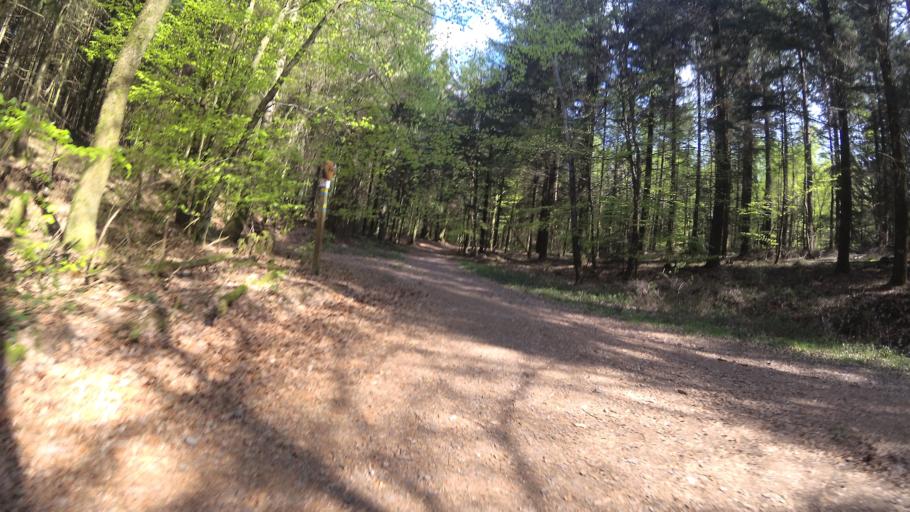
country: DE
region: Saarland
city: Mainzweiler
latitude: 49.4594
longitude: 7.1122
